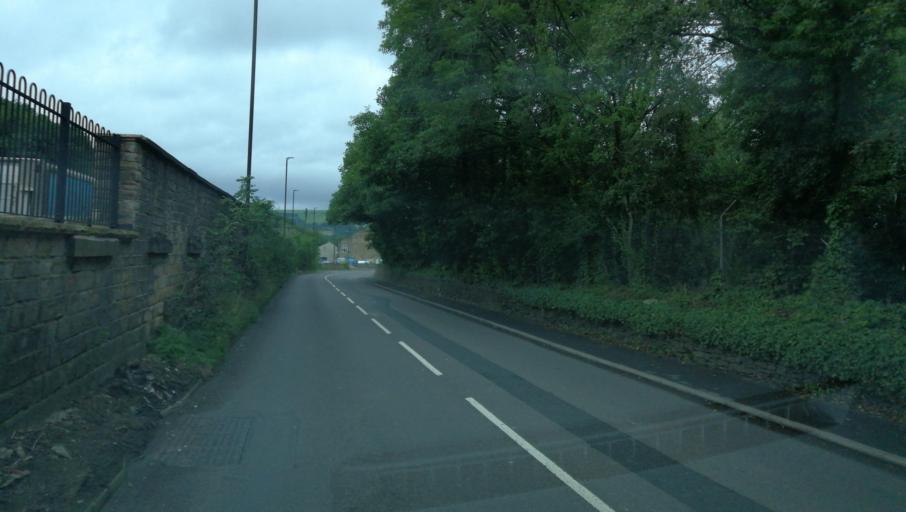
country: GB
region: England
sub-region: Derbyshire
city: Glossop
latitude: 53.4484
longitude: -1.9764
